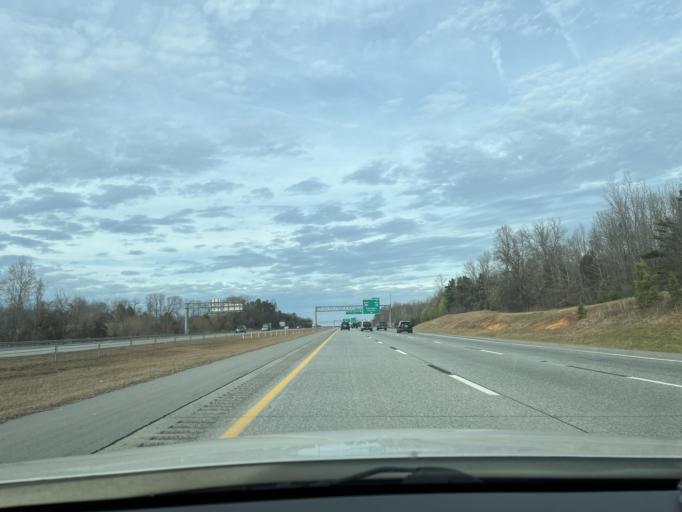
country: US
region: North Carolina
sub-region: Guilford County
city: Forest Oaks
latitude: 36.0428
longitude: -79.6887
